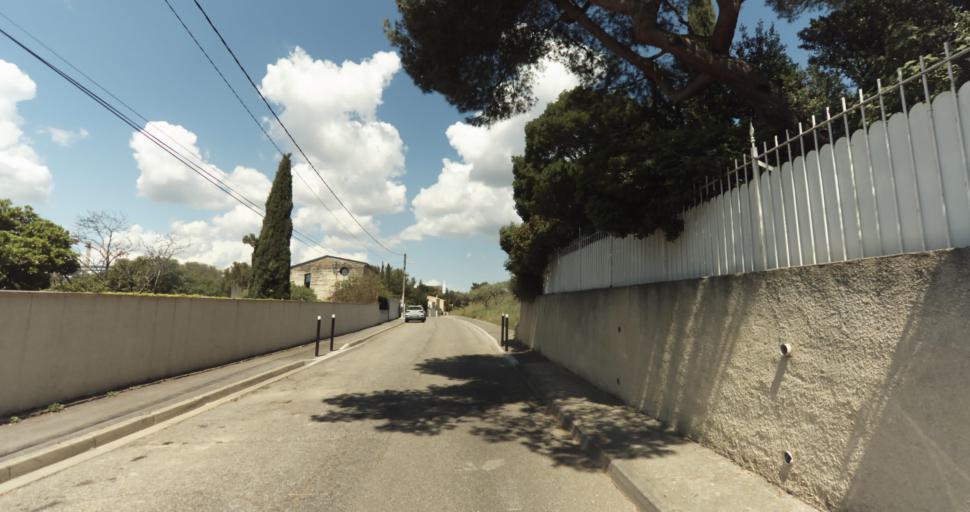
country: FR
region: Languedoc-Roussillon
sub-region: Departement du Gard
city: Nimes
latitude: 43.8191
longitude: 4.3266
